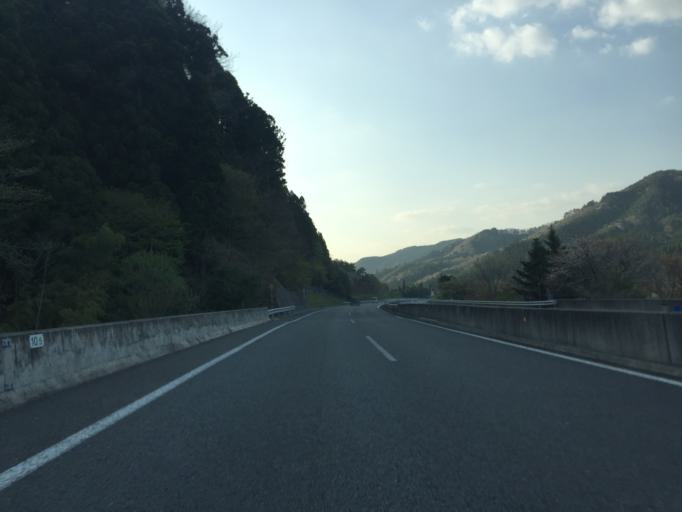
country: JP
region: Fukushima
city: Iwaki
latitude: 37.1115
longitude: 140.7545
